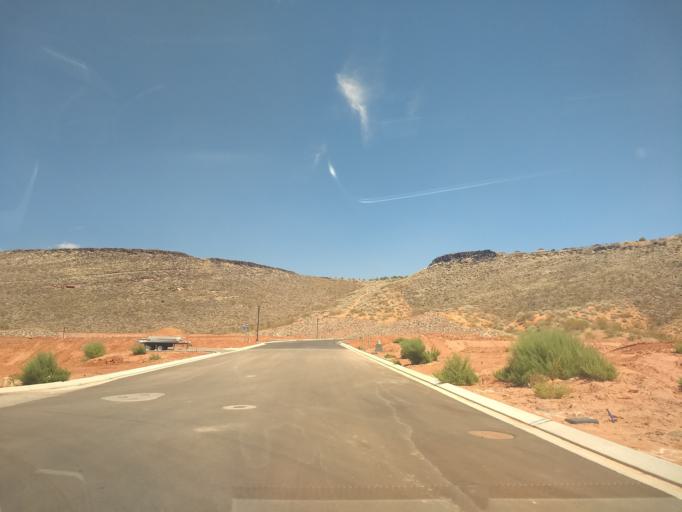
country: US
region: Utah
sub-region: Washington County
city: Washington
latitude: 37.1469
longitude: -113.4706
